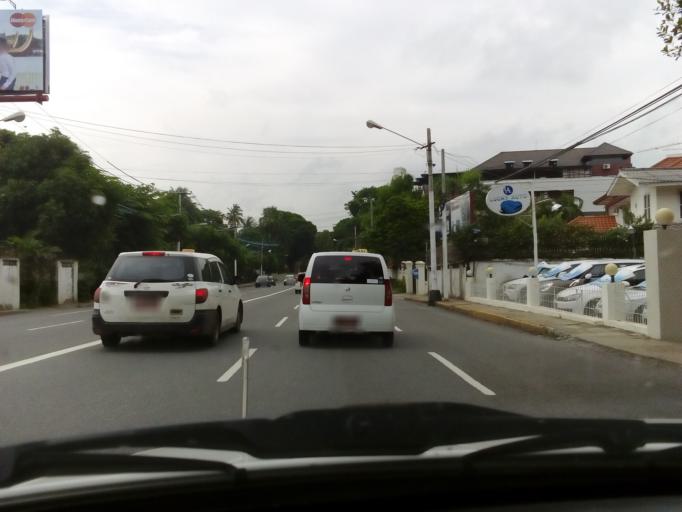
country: MM
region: Yangon
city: Yangon
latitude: 16.8211
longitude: 96.1550
